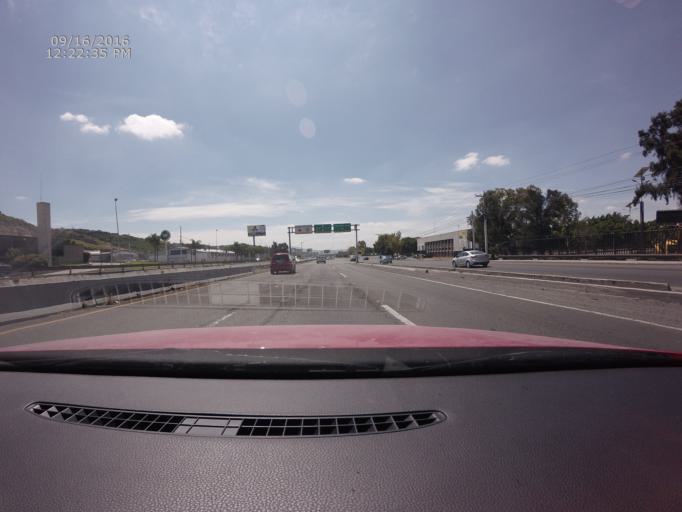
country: MX
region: Queretaro
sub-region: Queretaro
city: Sergio Villasenor
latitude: 20.6371
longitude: -100.4291
